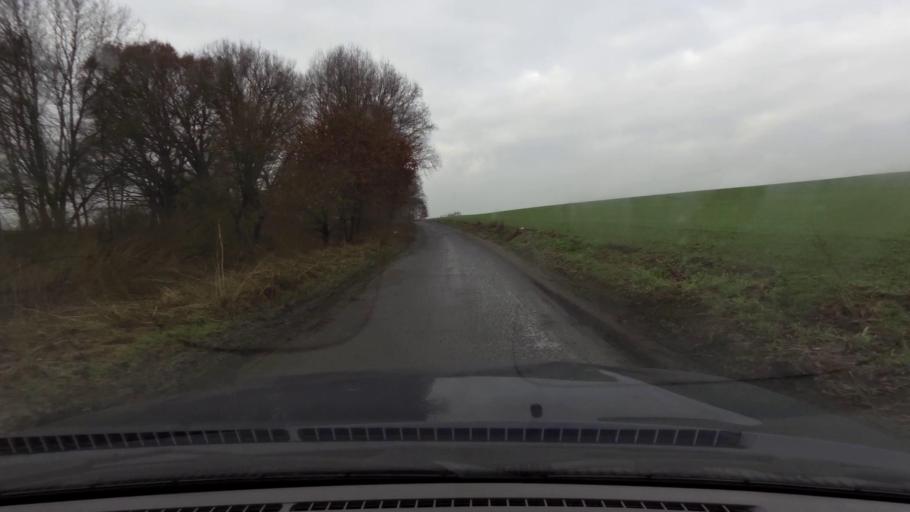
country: PL
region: West Pomeranian Voivodeship
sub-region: Powiat stargardzki
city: Stargard Szczecinski
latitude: 53.3340
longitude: 15.1292
